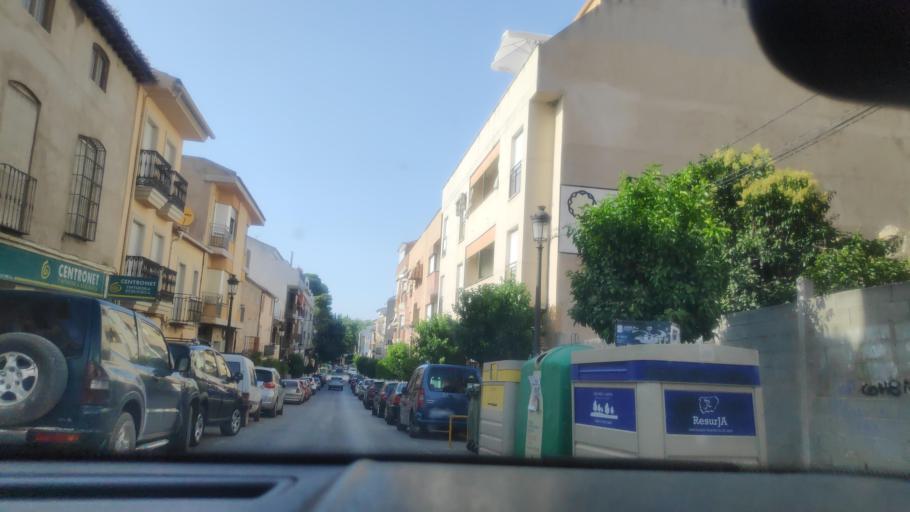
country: ES
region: Andalusia
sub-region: Provincia de Jaen
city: Mancha Real
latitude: 37.7867
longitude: -3.6093
